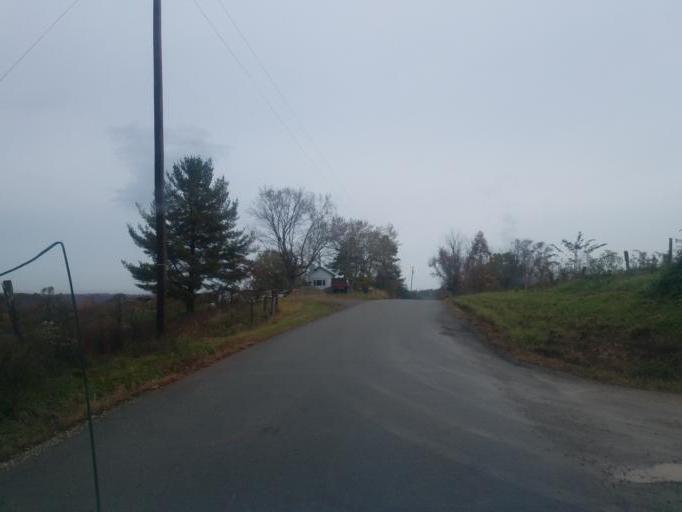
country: US
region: Ohio
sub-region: Washington County
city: Beverly
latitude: 39.5280
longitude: -81.7165
